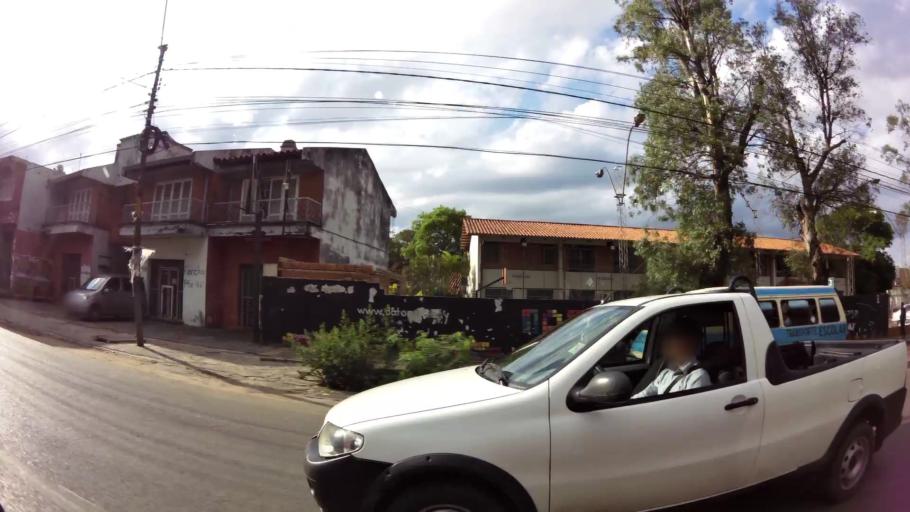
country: PY
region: Central
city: Fernando de la Mora
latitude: -25.2774
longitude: -57.5526
